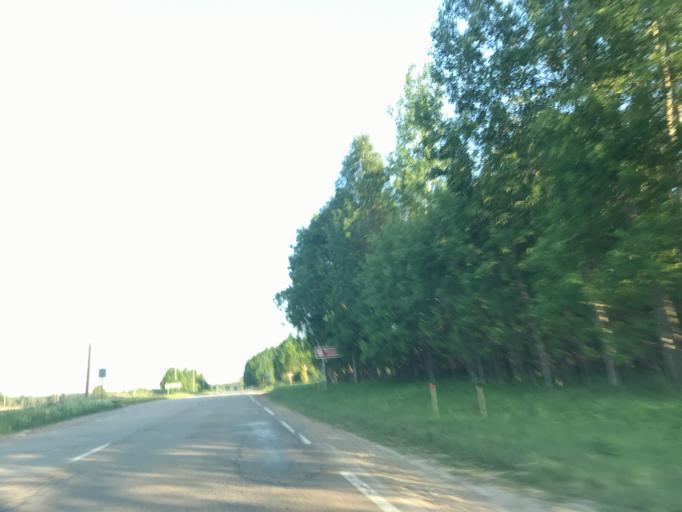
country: LV
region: Baldone
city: Baldone
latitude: 56.7046
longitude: 24.3776
